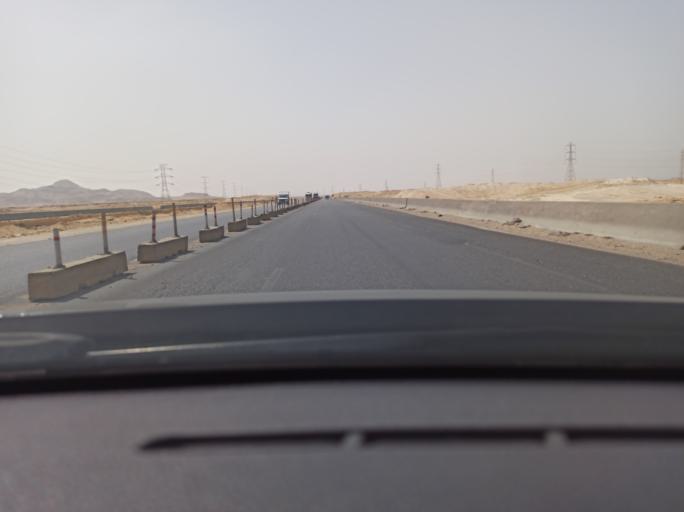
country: EG
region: Muhafazat Bani Suwayf
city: Bush
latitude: 29.1377
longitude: 31.2274
